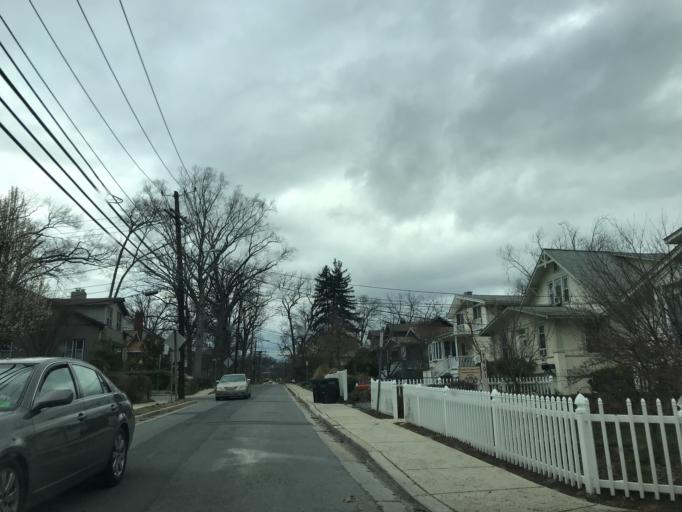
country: US
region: Maryland
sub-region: Montgomery County
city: Takoma Park
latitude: 38.9831
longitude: -76.9973
